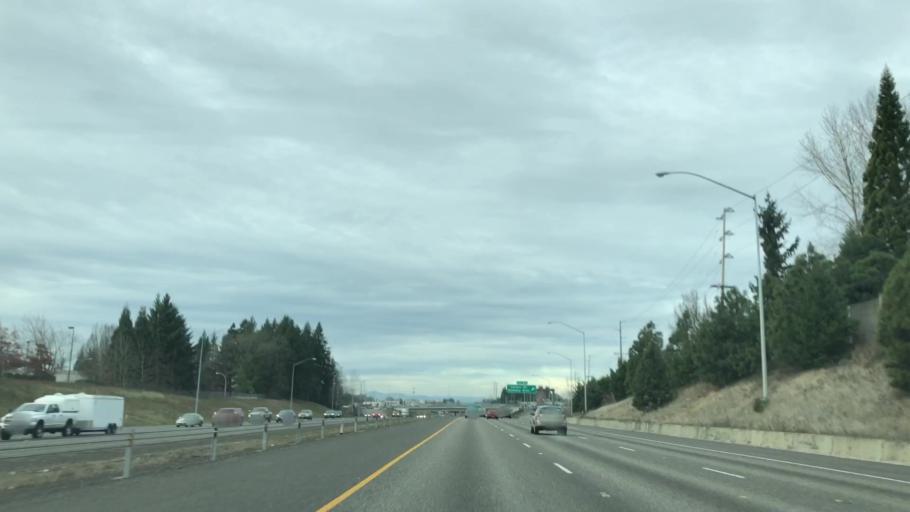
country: US
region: Oregon
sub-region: Washington County
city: Oak Hills
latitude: 45.5283
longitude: -122.8311
